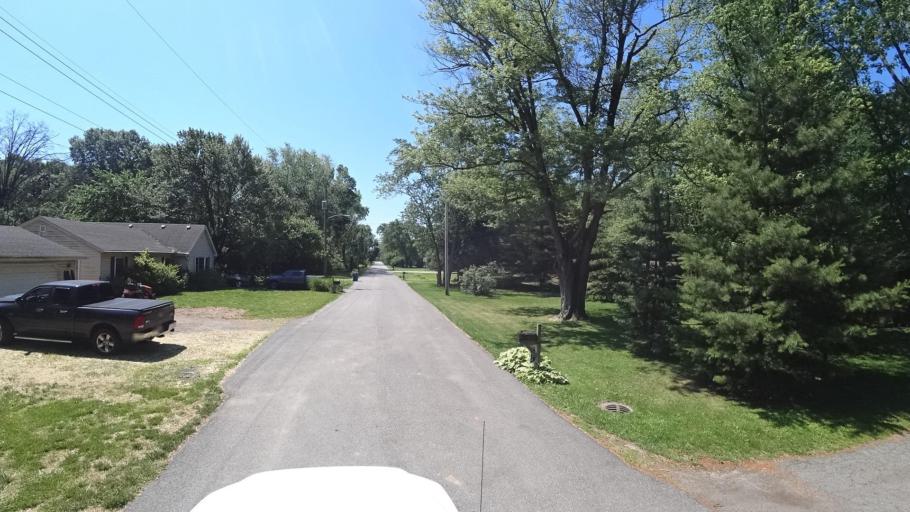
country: US
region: Indiana
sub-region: Porter County
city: Burns Harbor
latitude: 41.6139
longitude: -87.1138
